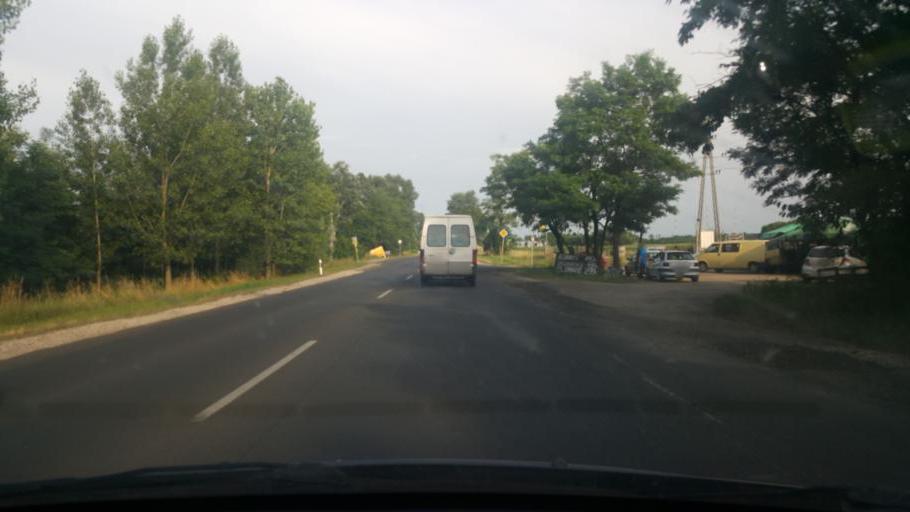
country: HU
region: Pest
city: Peteri
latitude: 47.3544
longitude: 19.4011
